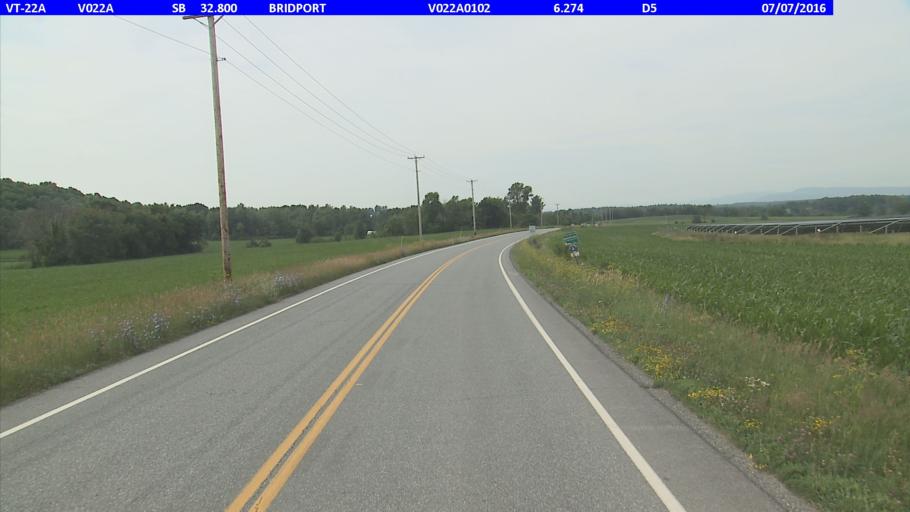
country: US
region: Vermont
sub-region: Addison County
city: Middlebury (village)
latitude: 44.0296
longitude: -73.3078
